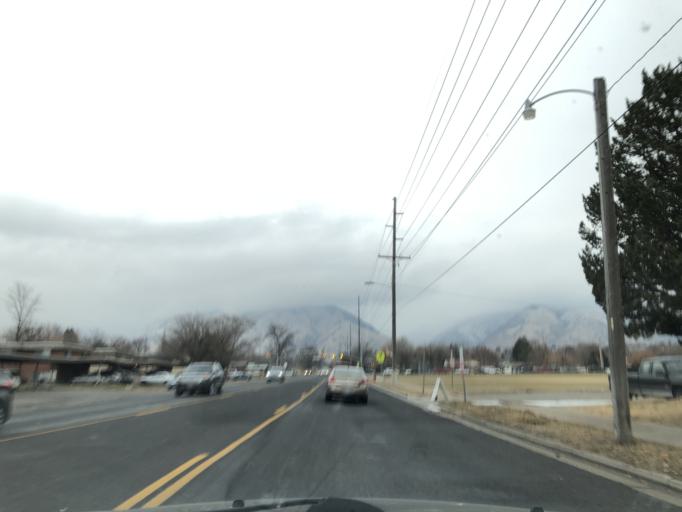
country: US
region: Utah
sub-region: Cache County
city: Logan
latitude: 41.7501
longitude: -111.8316
